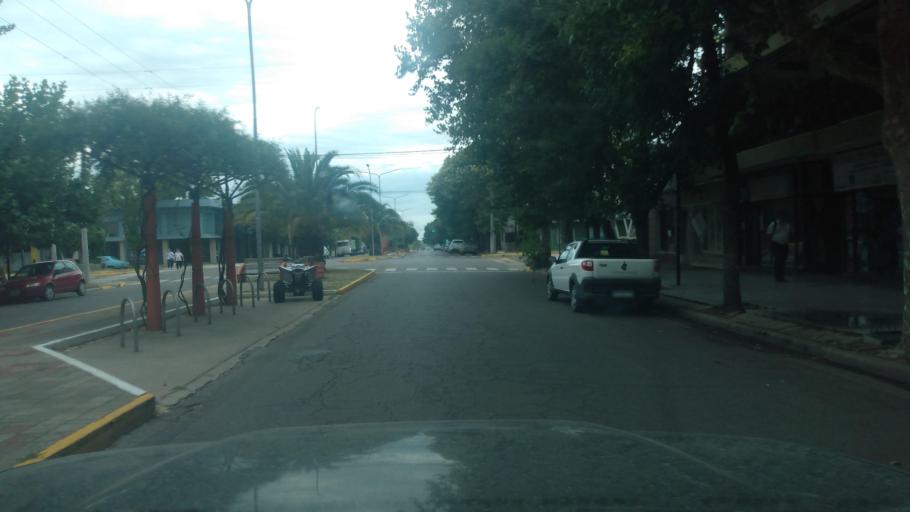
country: AR
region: Buenos Aires
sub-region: Partido de Trenque Lauquen
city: Trenque Lauquen
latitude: -35.9767
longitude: -62.7308
